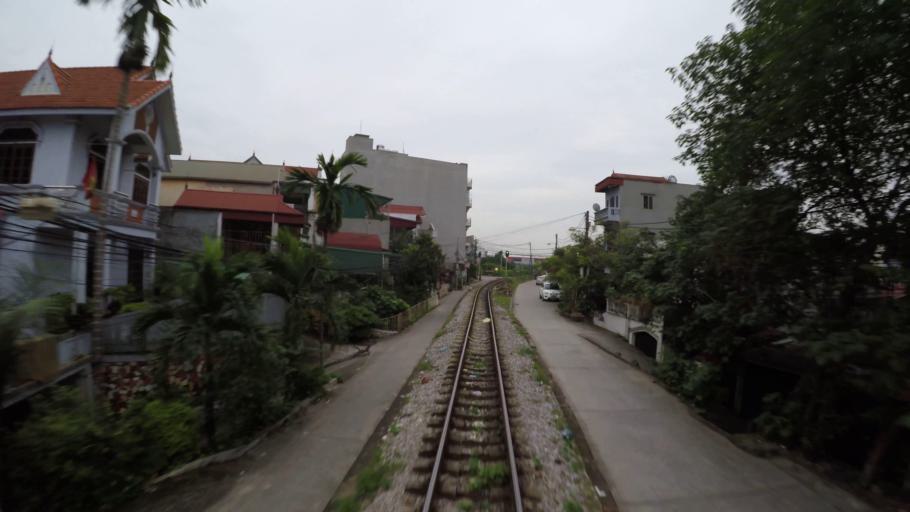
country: VN
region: Ha Noi
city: Trau Quy
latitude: 21.0205
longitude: 105.9387
